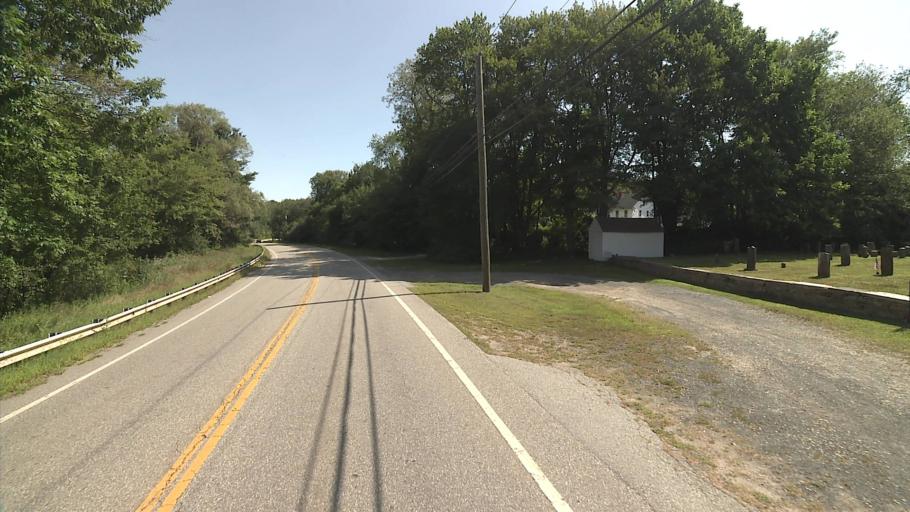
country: US
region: Connecticut
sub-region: New London County
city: Colchester
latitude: 41.6181
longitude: -72.2691
